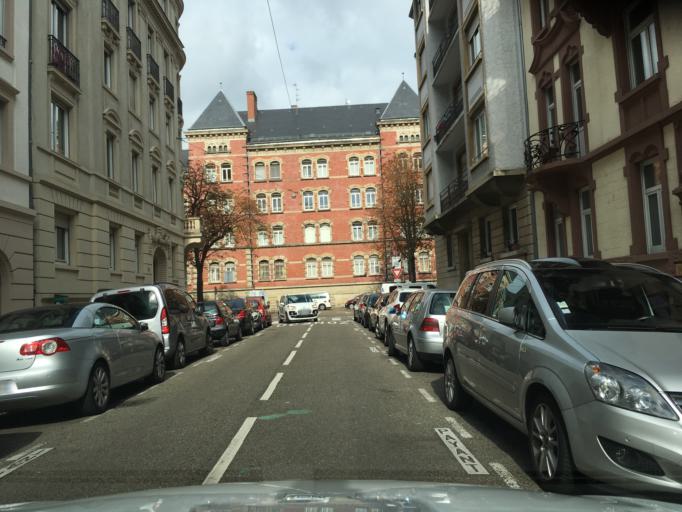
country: FR
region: Alsace
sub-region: Departement du Bas-Rhin
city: Strasbourg
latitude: 48.5912
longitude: 7.7510
